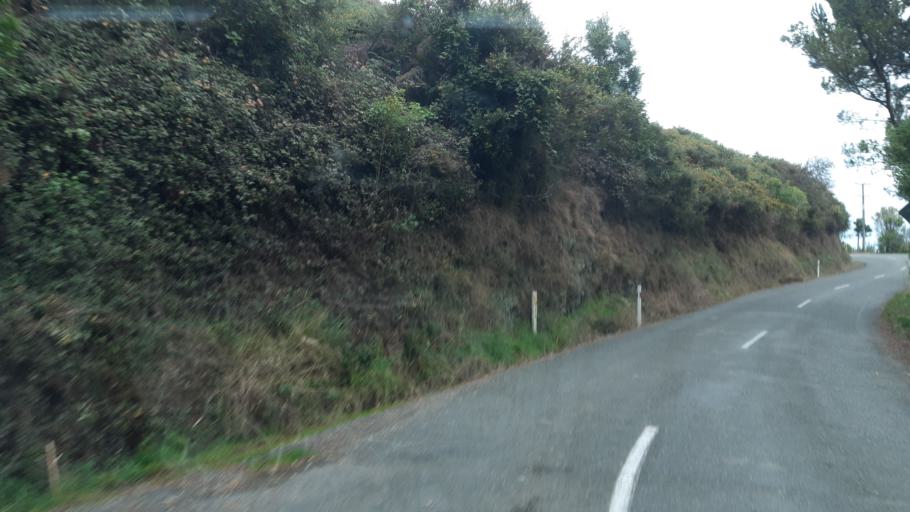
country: NZ
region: Nelson
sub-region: Nelson City
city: Nelson
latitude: -41.1656
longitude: 173.4161
